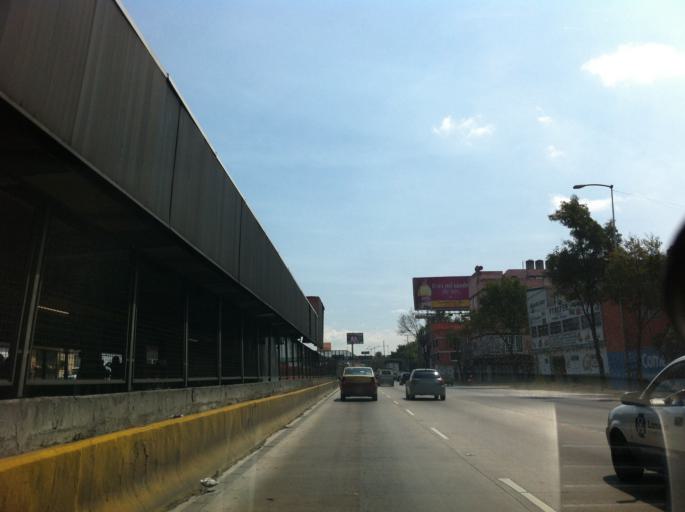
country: MX
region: Mexico City
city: Venustiano Carranza
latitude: 19.4519
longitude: -99.1070
